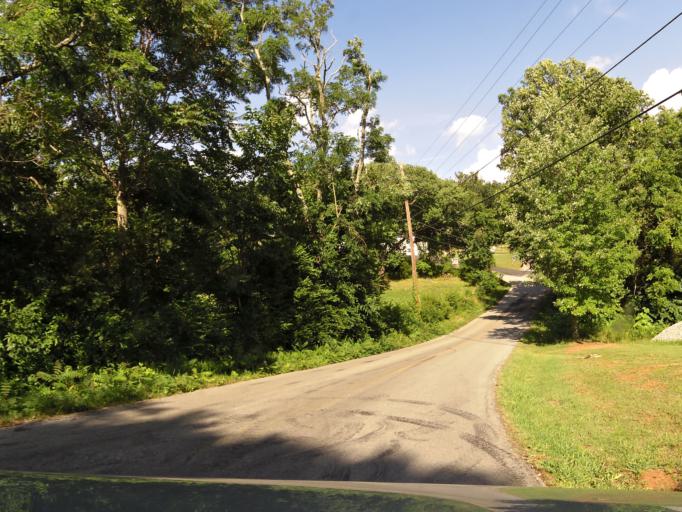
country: US
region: Tennessee
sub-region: Union County
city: Condon
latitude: 36.1405
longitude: -83.9114
